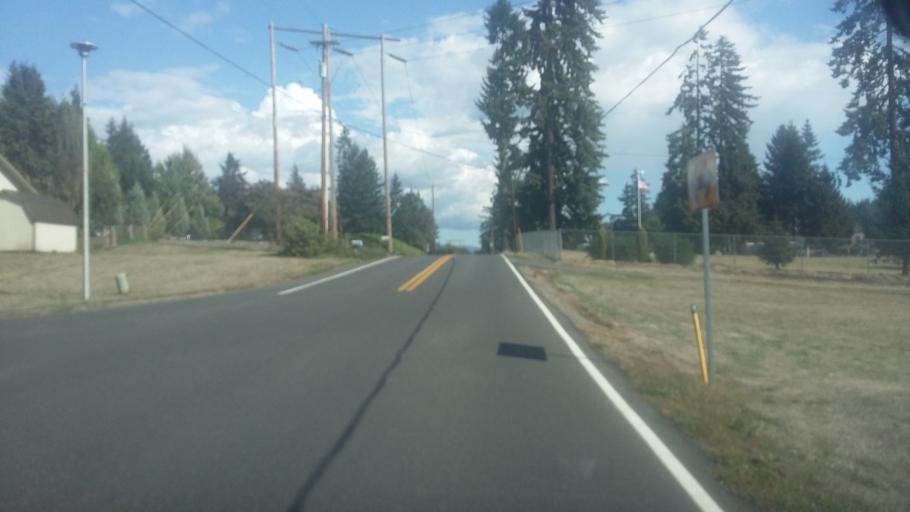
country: US
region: Washington
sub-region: Clark County
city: Barberton
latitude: 45.7004
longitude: -122.6105
